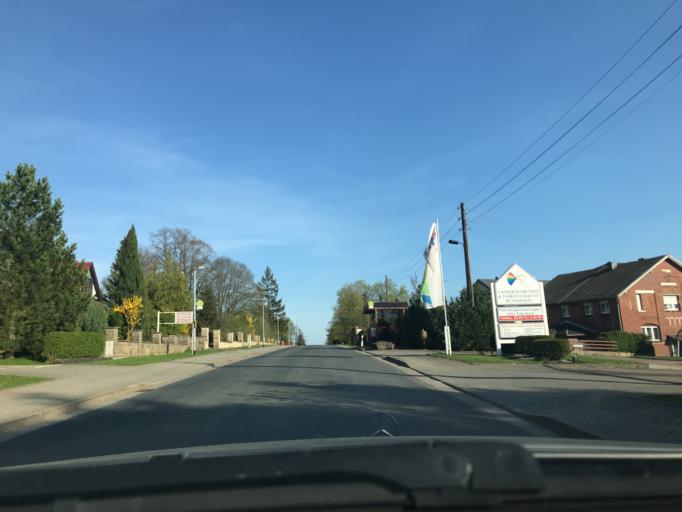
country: DE
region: Thuringia
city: Niederorschel
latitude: 51.3334
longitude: 10.4244
